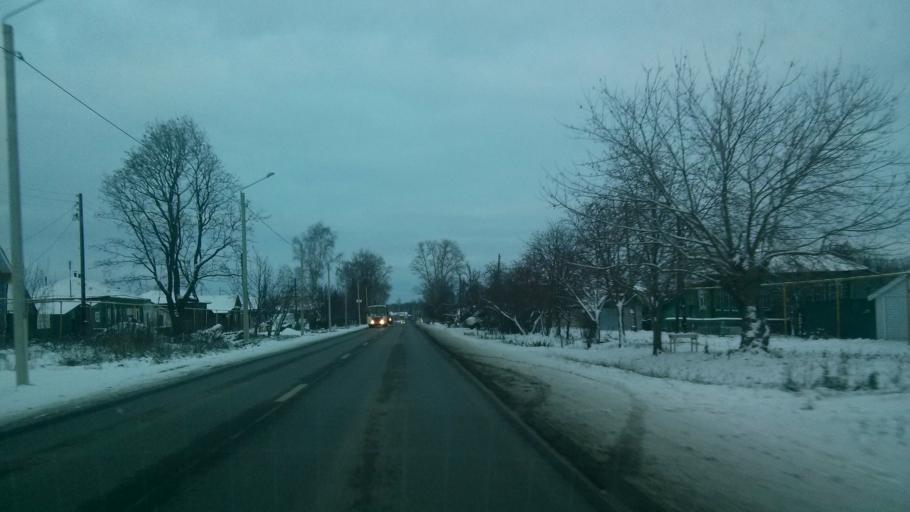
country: RU
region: Nizjnij Novgorod
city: Vorsma
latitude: 56.0336
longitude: 43.3654
